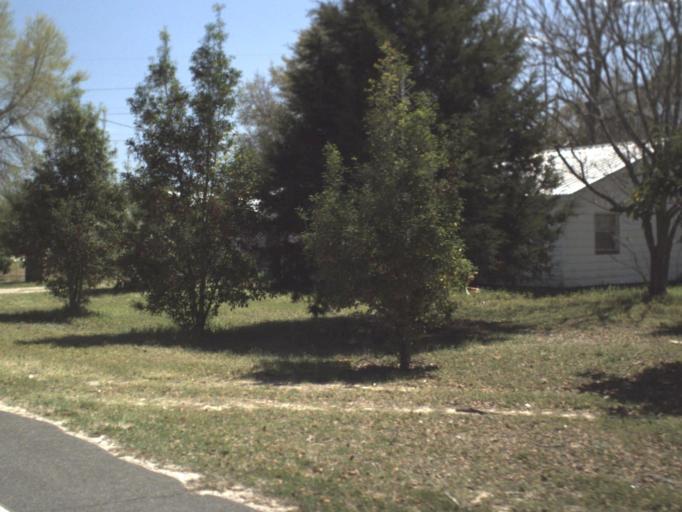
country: US
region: Florida
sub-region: Walton County
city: DeFuniak Springs
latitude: 30.7339
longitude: -85.9480
